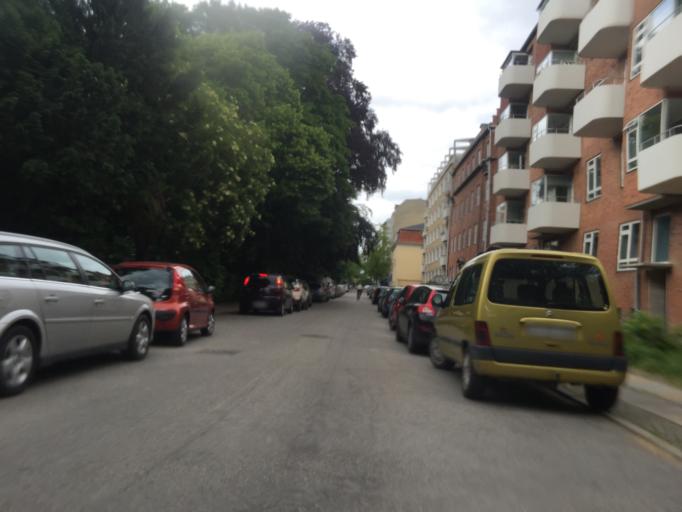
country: DK
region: Capital Region
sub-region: Frederiksberg Kommune
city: Frederiksberg
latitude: 55.6755
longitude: 12.5396
